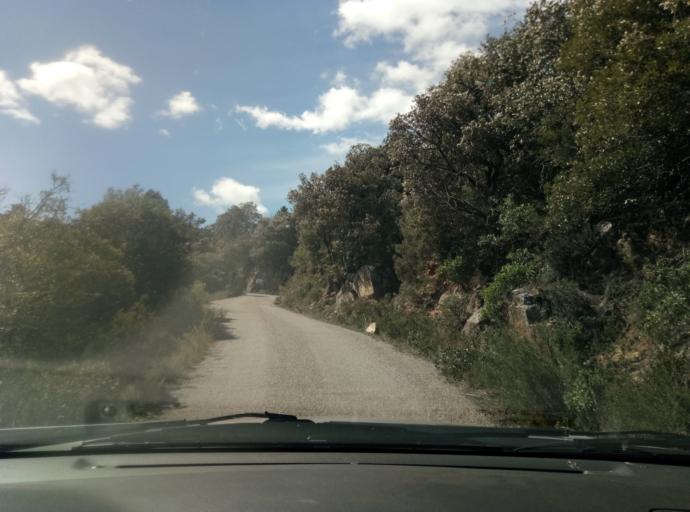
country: ES
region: Catalonia
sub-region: Provincia de Tarragona
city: Vimbodi
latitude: 41.3540
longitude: 1.0616
